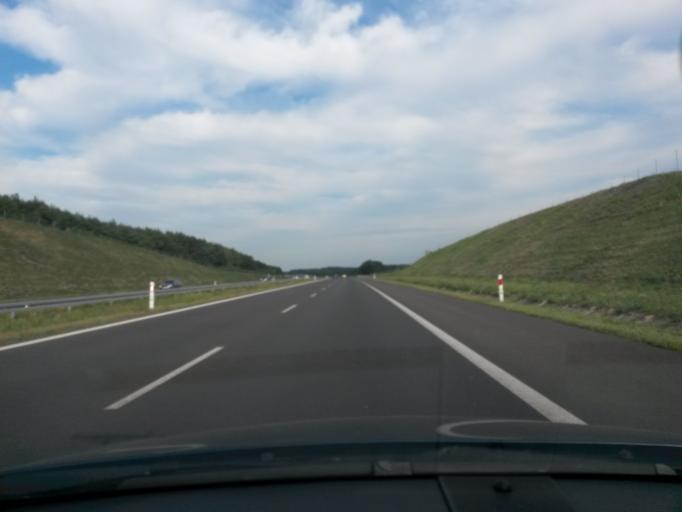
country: PL
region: Greater Poland Voivodeship
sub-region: Powiat kolski
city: Koscielec
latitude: 52.1436
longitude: 18.5198
